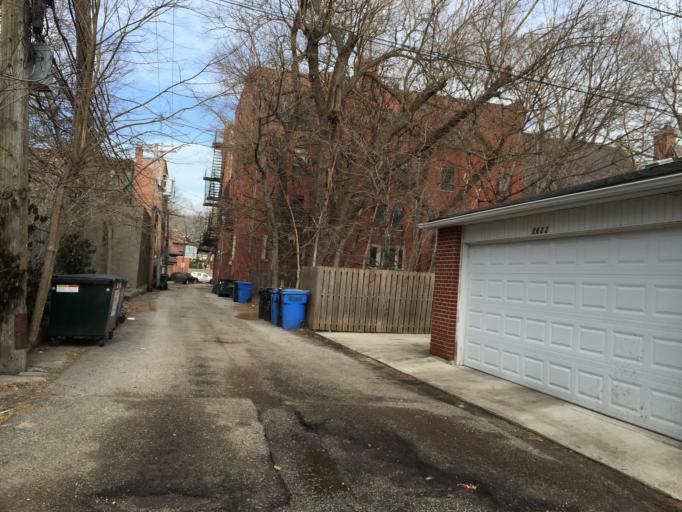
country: US
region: Illinois
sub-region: Cook County
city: Chicago
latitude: 41.7925
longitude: -87.5973
